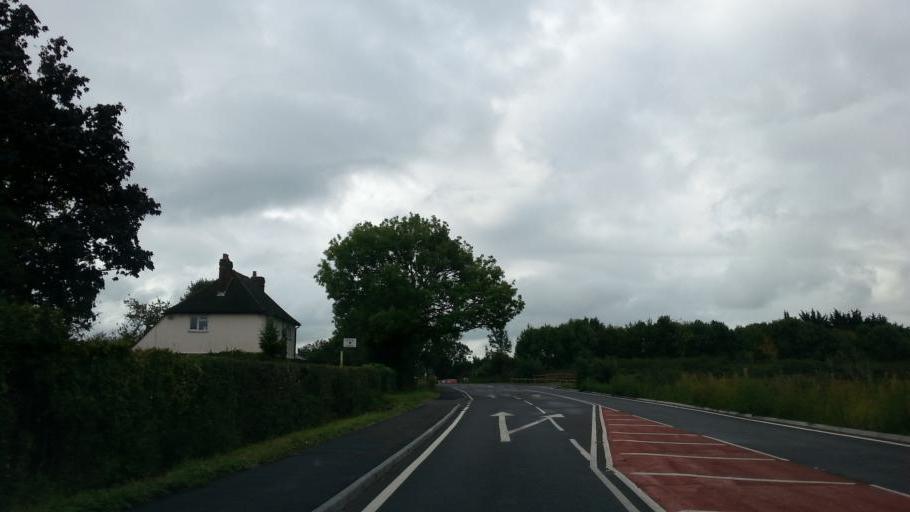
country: GB
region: England
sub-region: Hertfordshire
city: Hitchin
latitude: 51.9802
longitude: -0.2902
